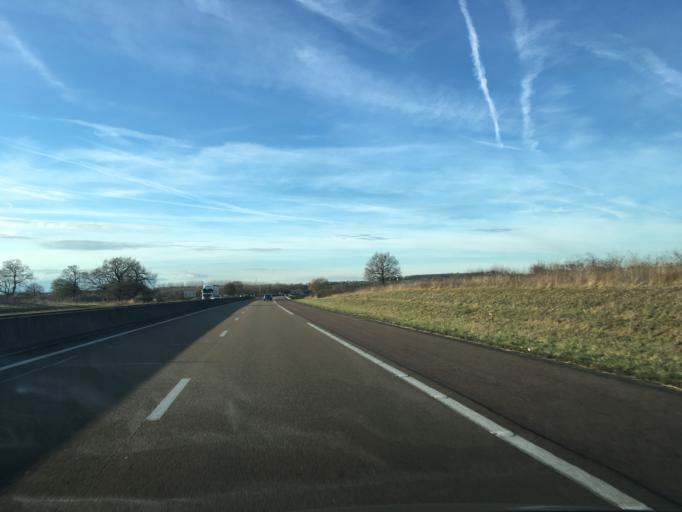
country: FR
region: Bourgogne
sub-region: Departement de l'Yonne
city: Avallon
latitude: 47.5055
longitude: 4.0144
